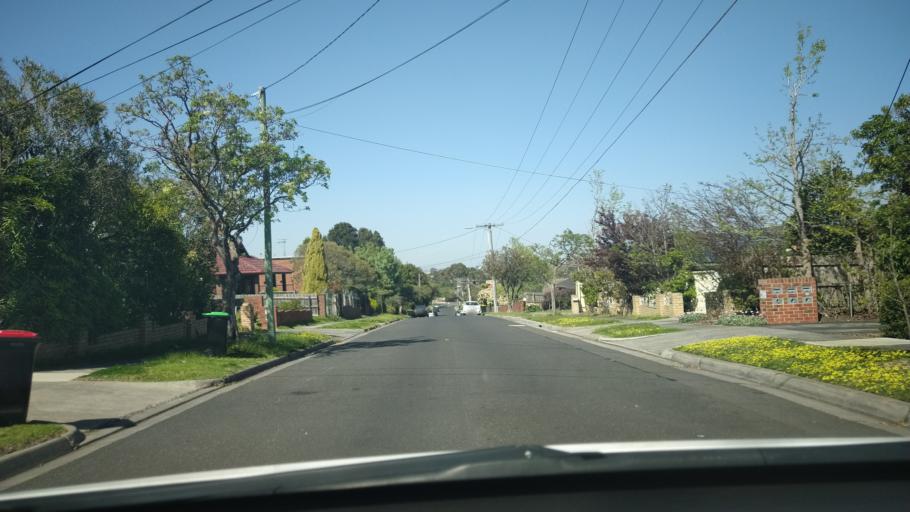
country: AU
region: Victoria
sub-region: Greater Dandenong
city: Noble Park
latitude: -37.9576
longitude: 145.1752
